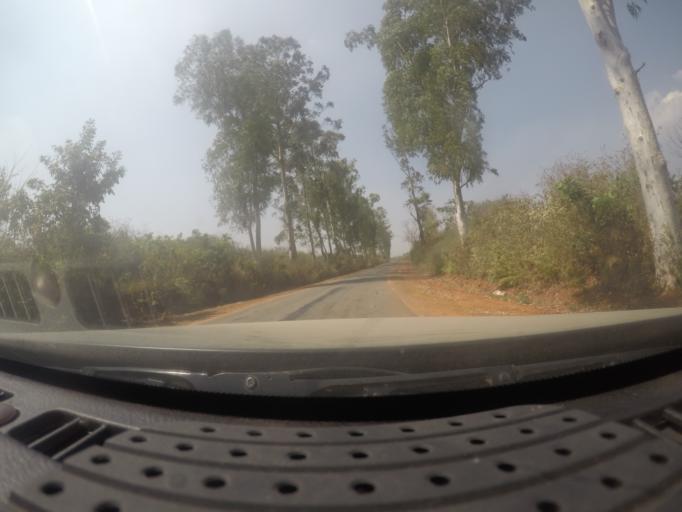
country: MM
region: Mandalay
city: Kyaukse
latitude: 21.1048
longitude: 96.4825
